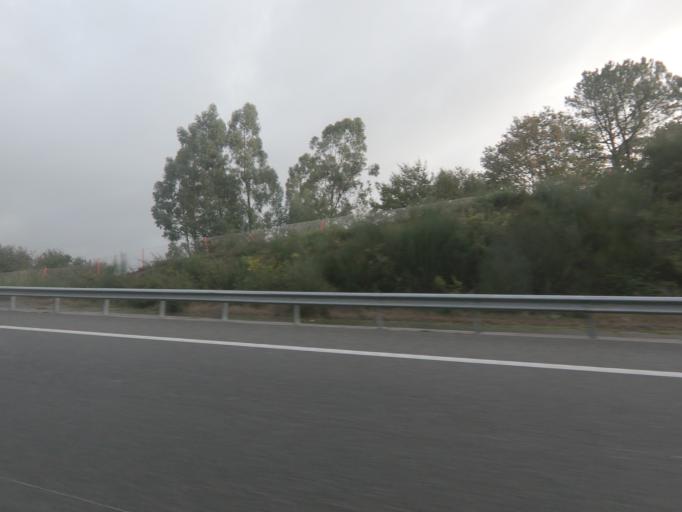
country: ES
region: Galicia
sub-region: Provincia de Pontevedra
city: Porrino
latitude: 42.1870
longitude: -8.6519
